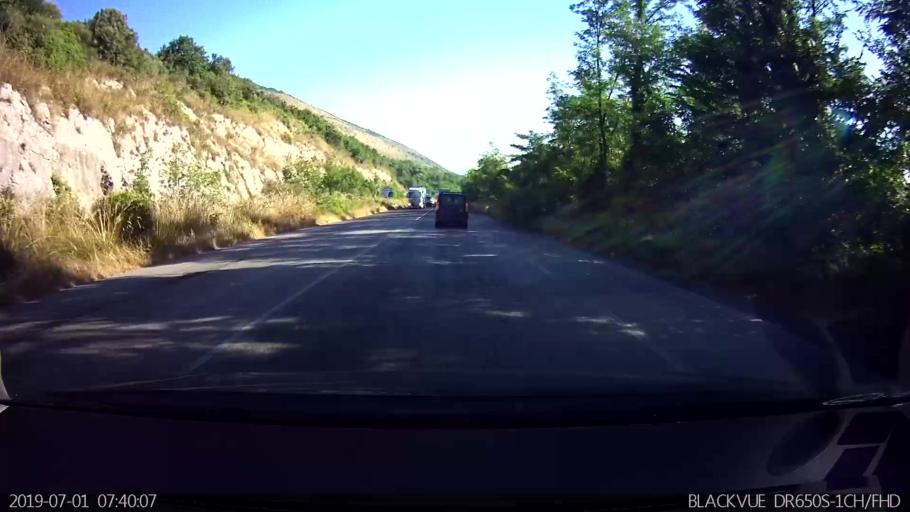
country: IT
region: Latium
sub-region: Provincia di Frosinone
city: Giuliano di Roma
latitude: 41.5550
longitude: 13.2665
